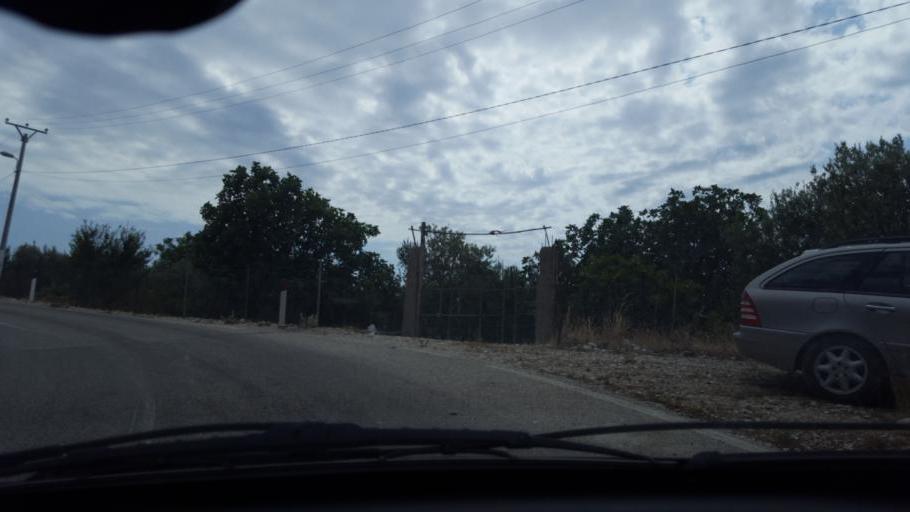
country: AL
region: Vlore
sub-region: Rrethi i Sarandes
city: Lukove
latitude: 40.0484
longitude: 19.8702
